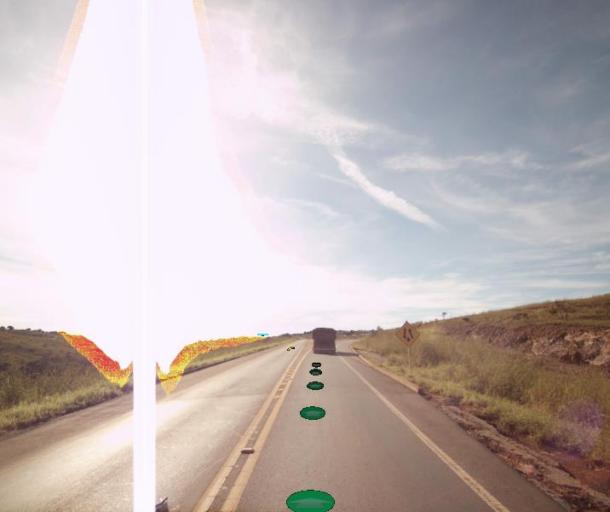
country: BR
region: Federal District
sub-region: Brasilia
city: Brasilia
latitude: -15.7550
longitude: -48.3406
